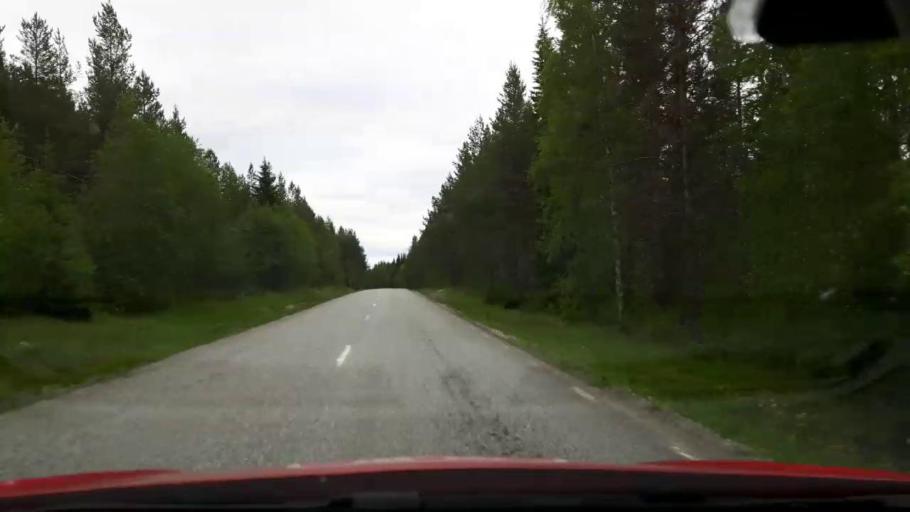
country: SE
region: Jaemtland
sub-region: Ragunda Kommun
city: Hammarstrand
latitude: 63.2398
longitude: 15.9154
